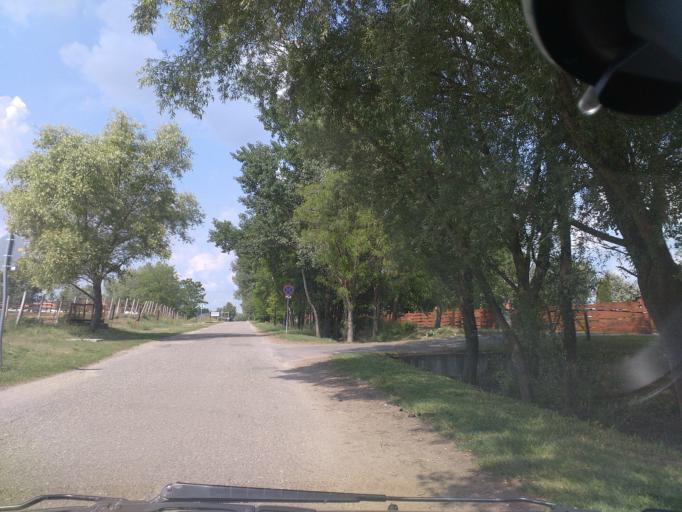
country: HU
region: Pest
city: Veresegyhaz
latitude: 47.6341
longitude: 19.2593
